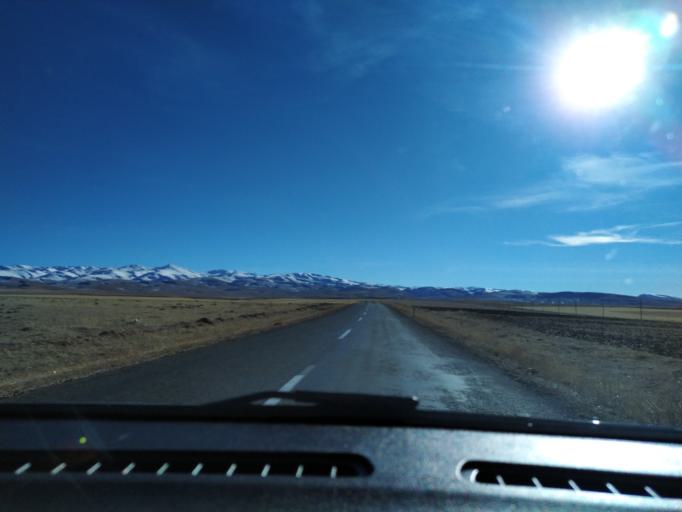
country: TR
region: Kayseri
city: Orensehir
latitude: 38.8950
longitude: 36.7292
